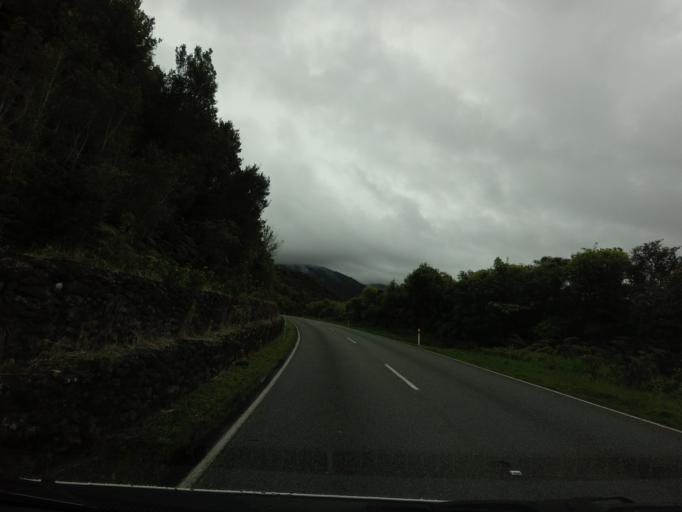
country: NZ
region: West Coast
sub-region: Westland District
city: Hokitika
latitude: -42.8934
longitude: 170.8238
